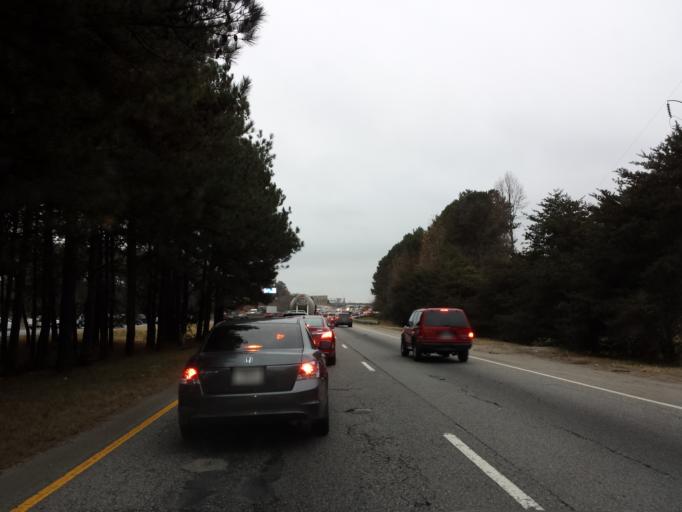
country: US
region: Georgia
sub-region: Clayton County
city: Forest Park
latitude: 33.6252
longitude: -84.4007
